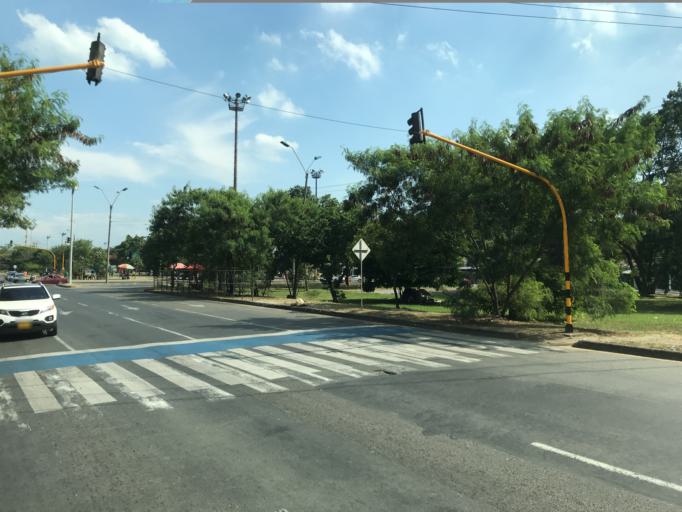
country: CO
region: Valle del Cauca
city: Cali
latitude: 3.4875
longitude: -76.4993
